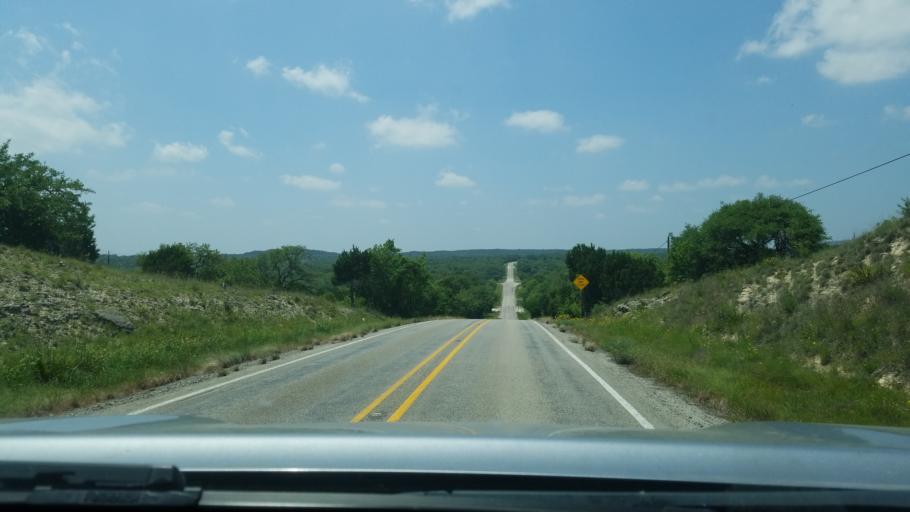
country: US
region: Texas
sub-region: Hays County
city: Woodcreek
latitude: 30.0985
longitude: -98.2457
